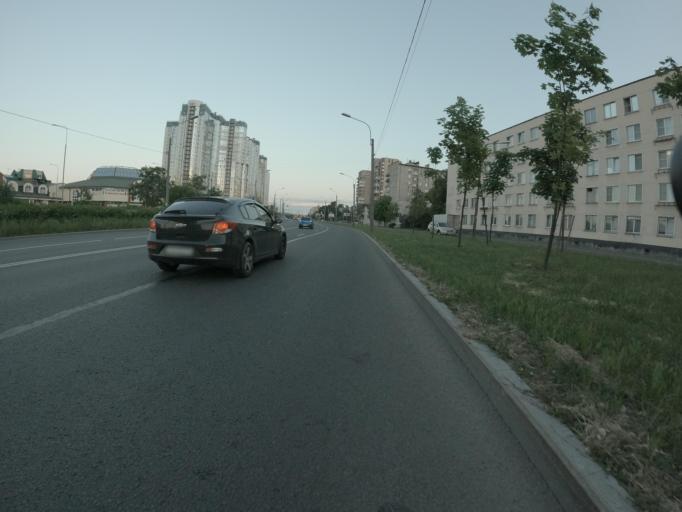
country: RU
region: St.-Petersburg
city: Avtovo
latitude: 59.8535
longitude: 30.2804
